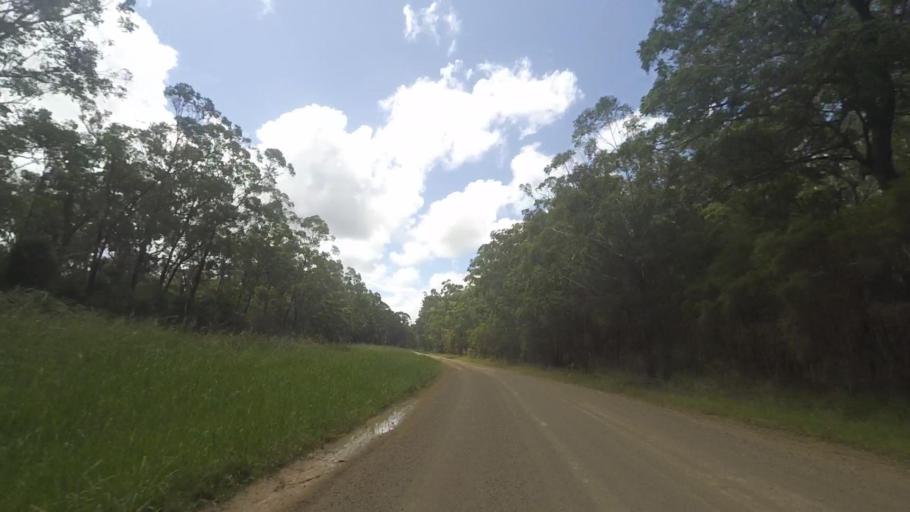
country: AU
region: New South Wales
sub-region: Great Lakes
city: Bulahdelah
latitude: -32.4970
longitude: 152.2784
